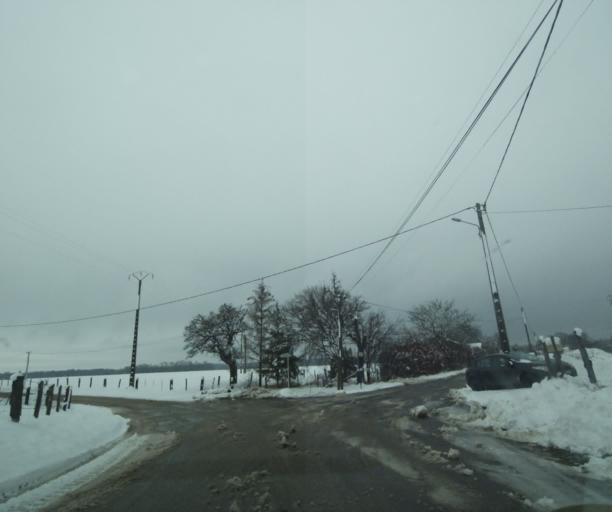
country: FR
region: Champagne-Ardenne
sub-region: Departement de la Haute-Marne
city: Montier-en-Der
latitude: 48.5109
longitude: 4.7797
